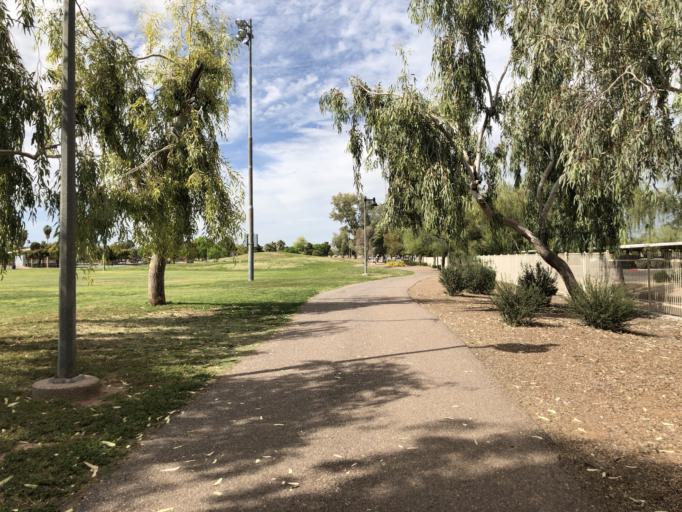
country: US
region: Arizona
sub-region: Maricopa County
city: Guadalupe
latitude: 33.3110
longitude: -111.9186
